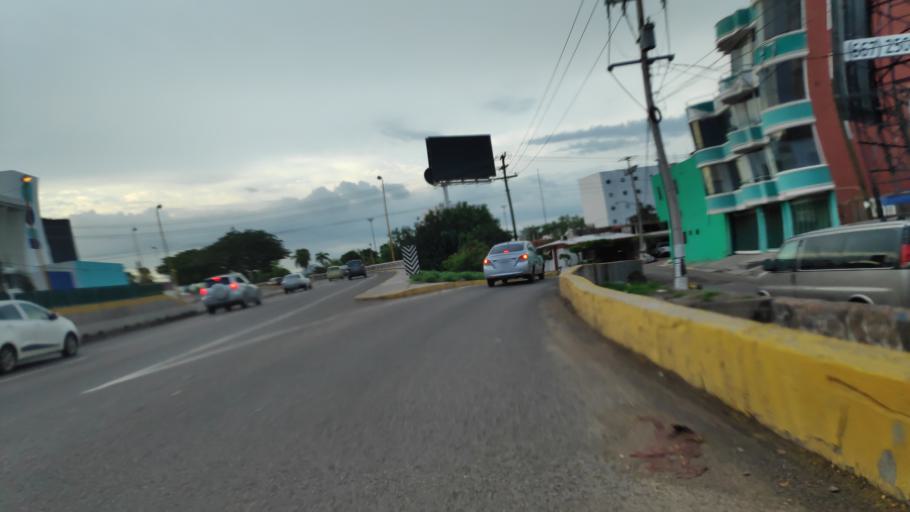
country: MX
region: Sinaloa
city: Culiacan
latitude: 24.8071
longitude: -107.4060
